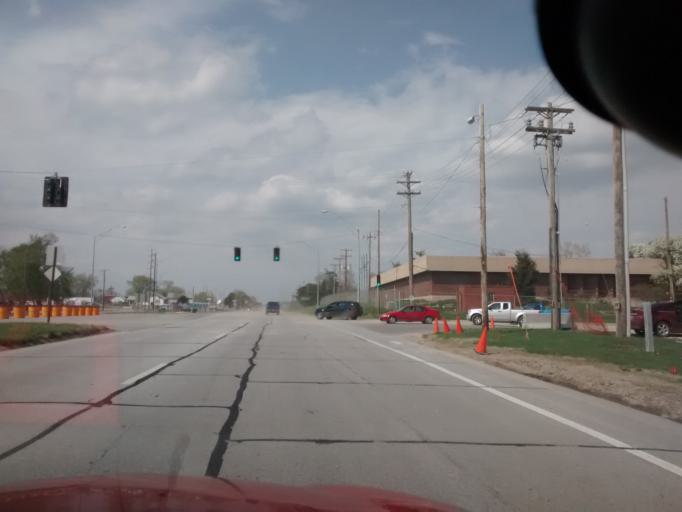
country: US
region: Nebraska
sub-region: Sarpy County
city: Offutt Air Force Base
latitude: 41.1181
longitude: -95.9265
